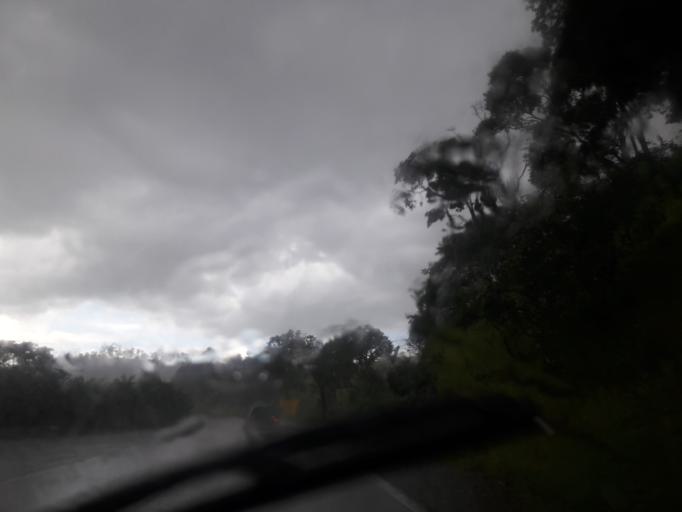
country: BR
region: Sao Paulo
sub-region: Bom Jesus Dos Perdoes
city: Bom Jesus dos Perdoes
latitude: -23.1903
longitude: -46.3991
